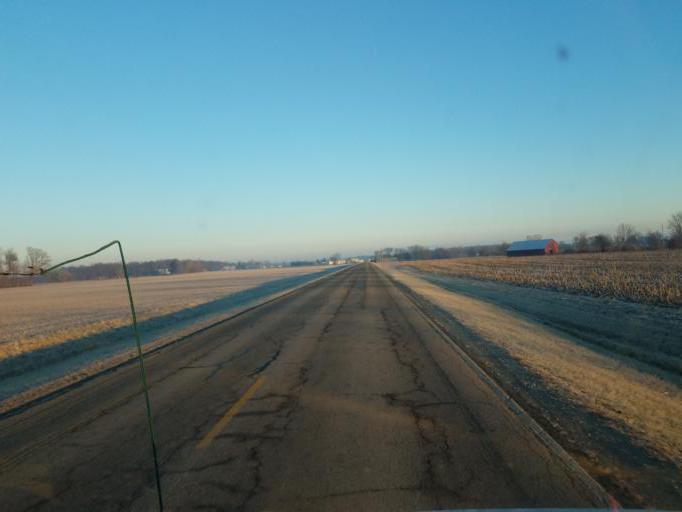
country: US
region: Ohio
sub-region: Marion County
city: Marion
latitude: 40.5391
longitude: -83.0764
